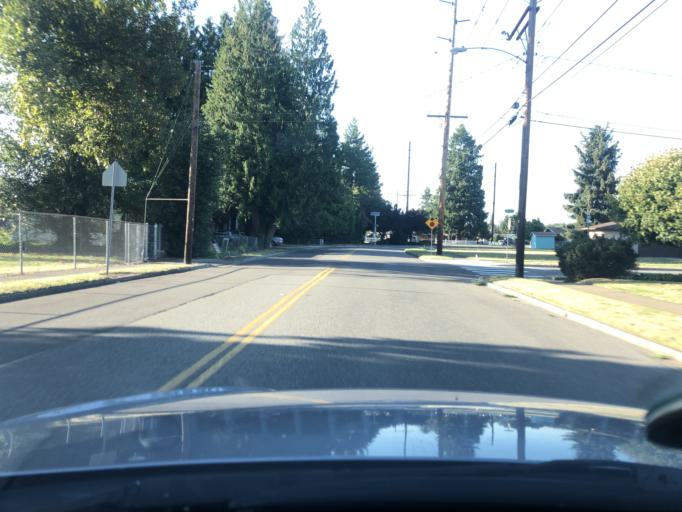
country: US
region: Washington
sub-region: King County
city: Auburn
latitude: 47.2889
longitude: -122.2134
